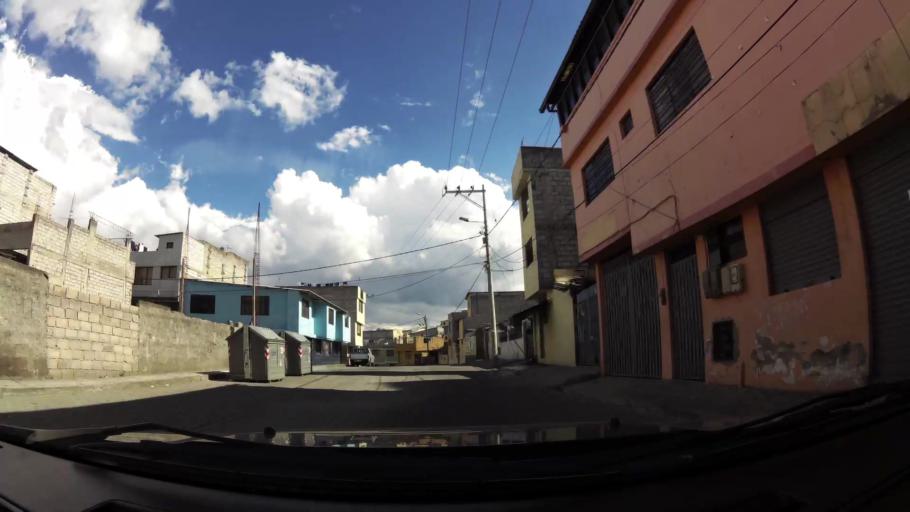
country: EC
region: Pichincha
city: Quito
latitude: -0.1228
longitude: -78.4711
